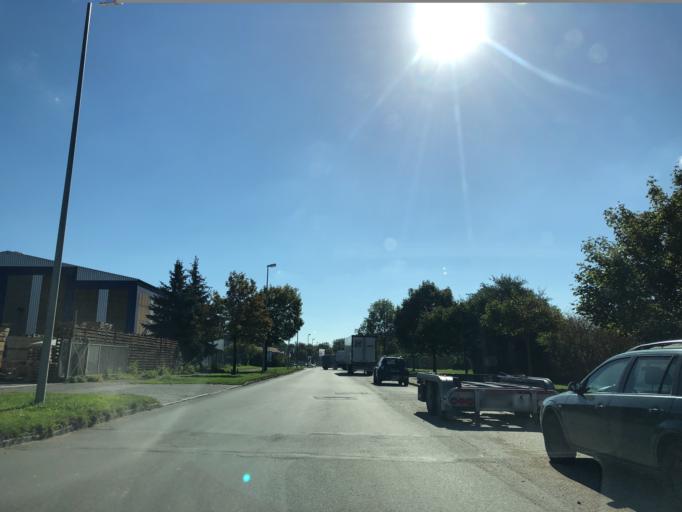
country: DE
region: Baden-Wuerttemberg
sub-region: Tuebingen Region
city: Ulm
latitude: 48.3632
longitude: 9.9528
